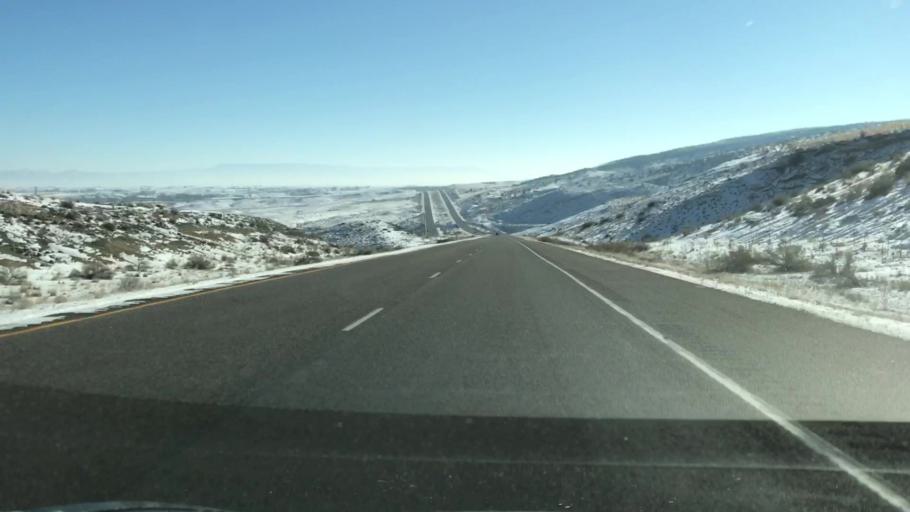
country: US
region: Colorado
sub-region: Mesa County
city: Loma
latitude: 39.2276
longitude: -108.9013
